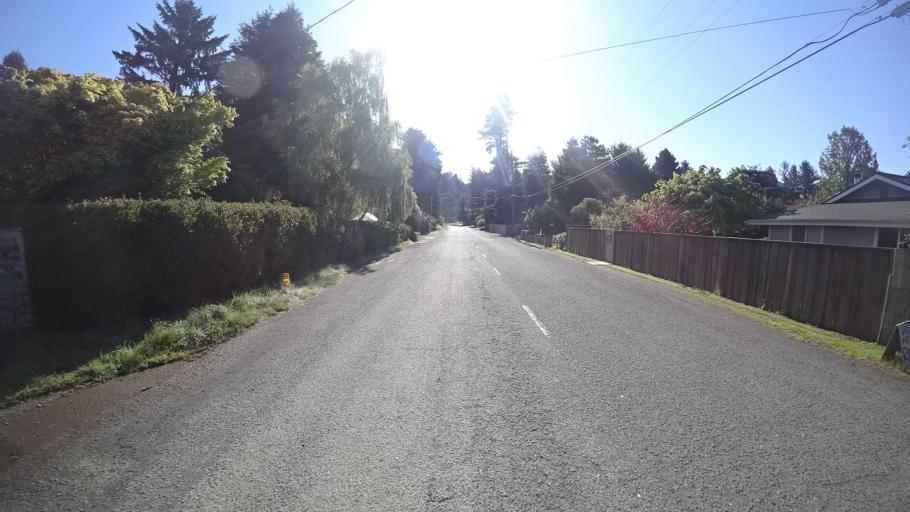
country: US
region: California
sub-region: Humboldt County
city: Westhaven-Moonstone
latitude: 41.0358
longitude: -124.1096
